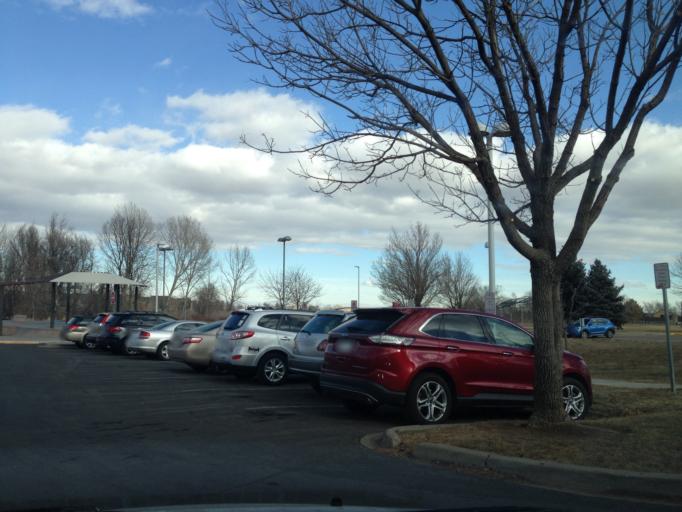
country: US
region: Colorado
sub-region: Boulder County
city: Lafayette
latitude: 40.0015
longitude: -105.0909
